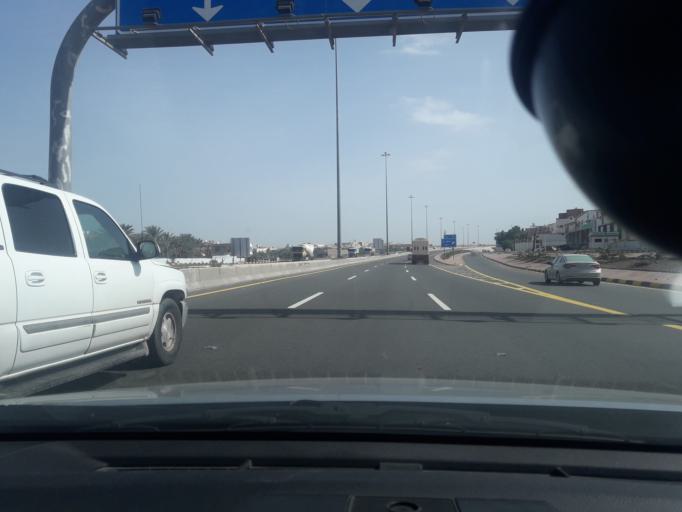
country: SA
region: Al Madinah al Munawwarah
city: Medina
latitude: 24.4427
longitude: 39.6342
